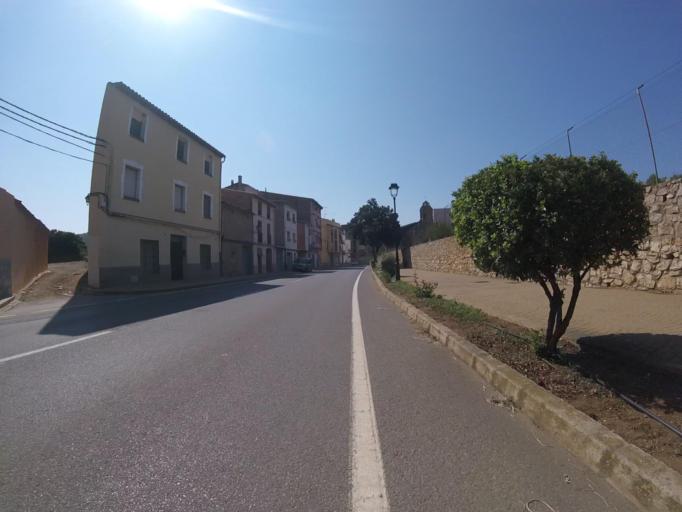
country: ES
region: Valencia
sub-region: Provincia de Castello
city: Adzaneta
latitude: 40.2182
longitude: -0.1703
